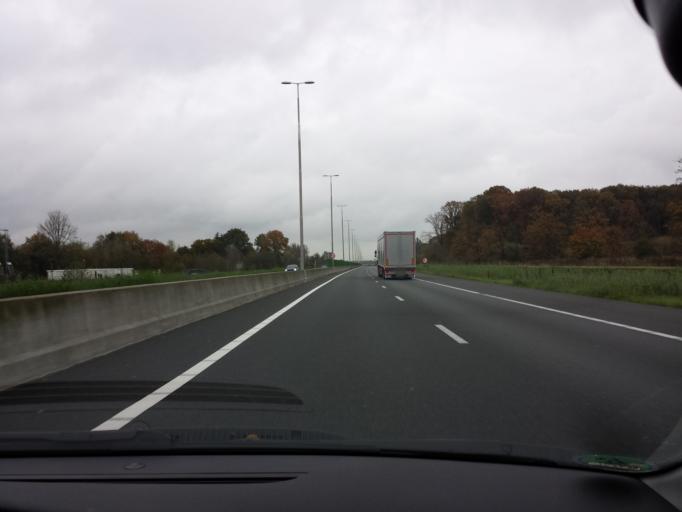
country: NL
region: Limburg
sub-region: Gemeente Venlo
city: Tegelen
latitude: 51.3272
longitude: 6.1428
